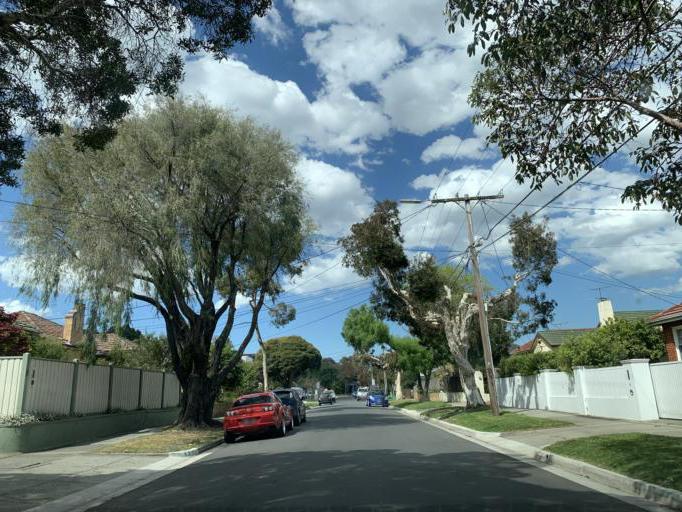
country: AU
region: Victoria
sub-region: Bayside
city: Highett
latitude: -37.9540
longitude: 145.0432
